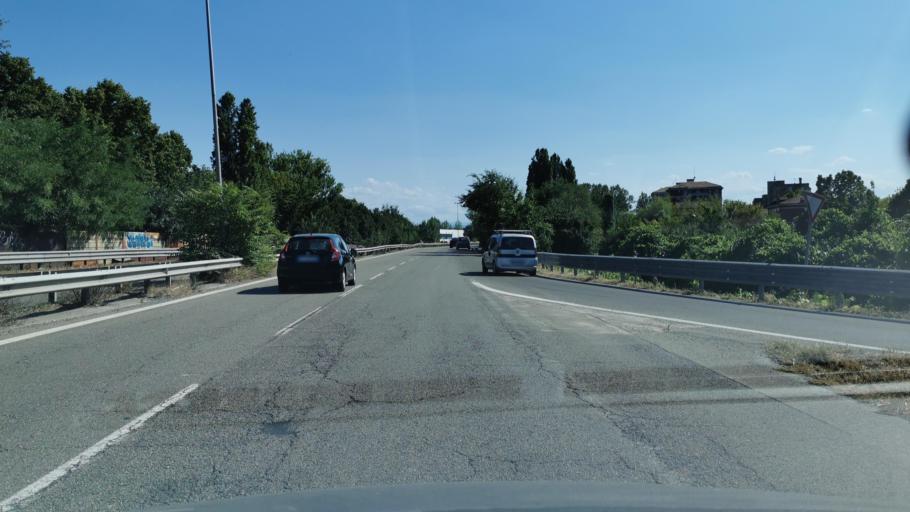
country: IT
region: Emilia-Romagna
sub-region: Provincia di Modena
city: Modena
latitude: 44.6415
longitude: 10.9610
